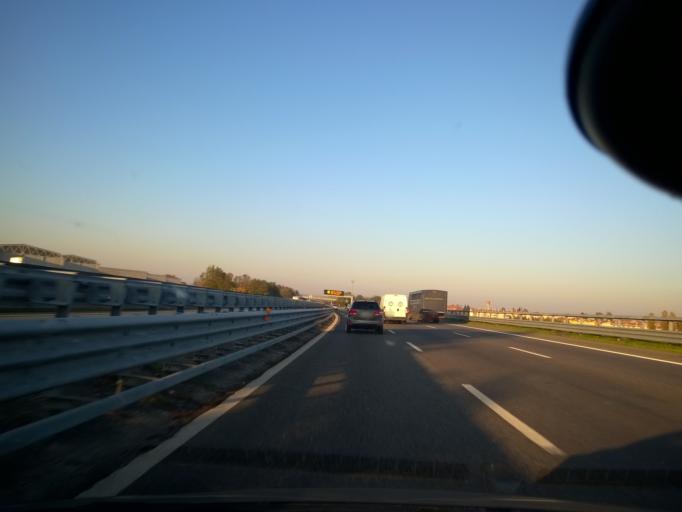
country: IT
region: Lombardy
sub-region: Citta metropolitana di Milano
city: Binasco
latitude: 45.3230
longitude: 9.0880
